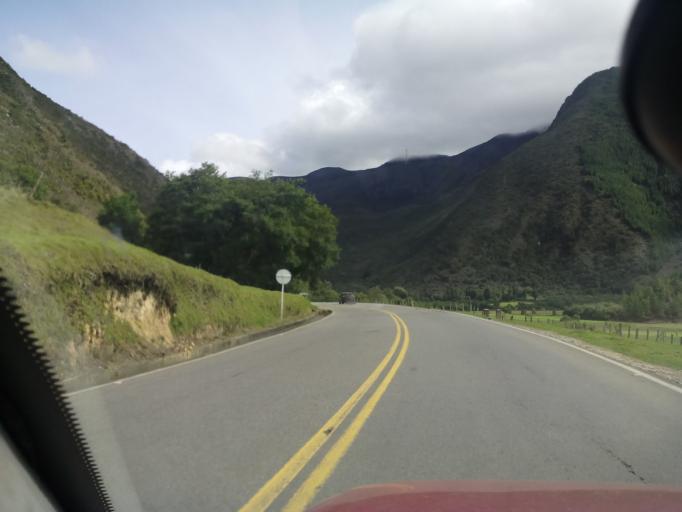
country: CO
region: Boyaca
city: Arcabuco
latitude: 5.7172
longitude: -73.3751
